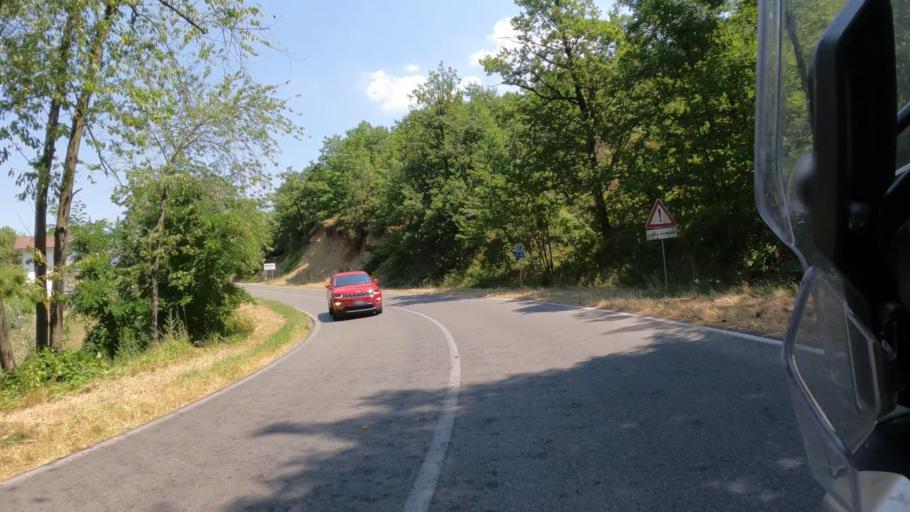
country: IT
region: Piedmont
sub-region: Provincia di Alessandria
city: Ponzone
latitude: 44.5541
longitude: 8.4911
